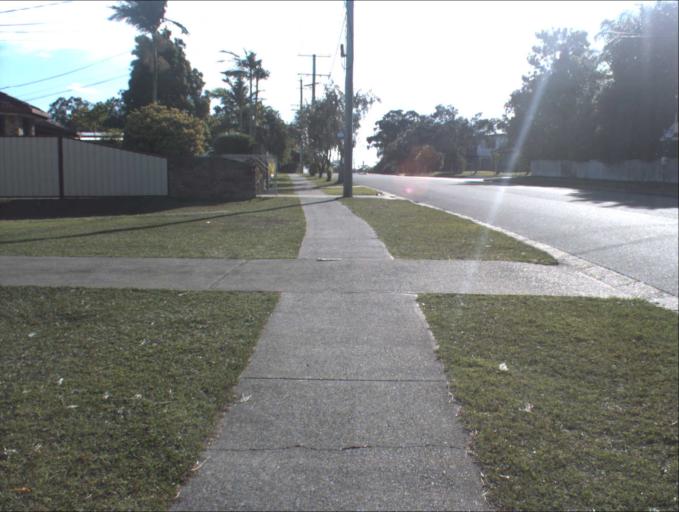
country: AU
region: Queensland
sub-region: Logan
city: Waterford West
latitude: -27.6761
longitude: 153.1039
